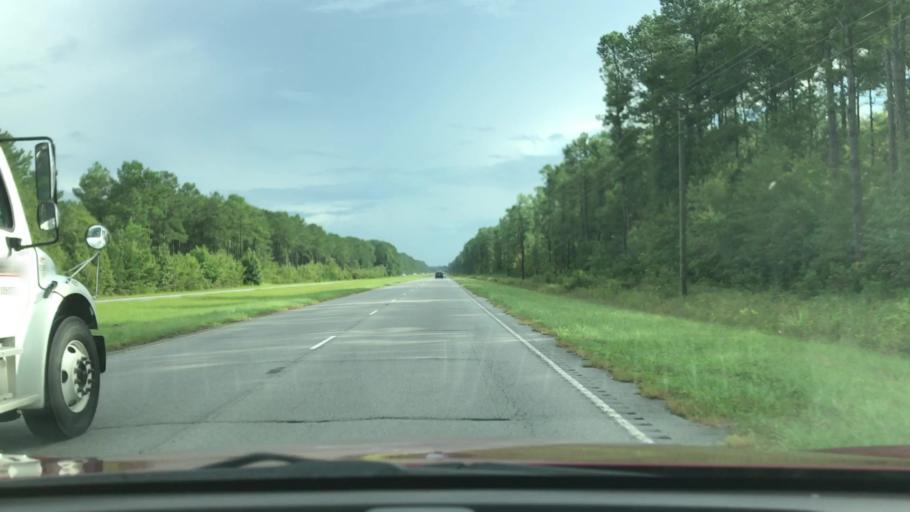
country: US
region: South Carolina
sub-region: Charleston County
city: Awendaw
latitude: 33.0094
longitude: -79.6390
